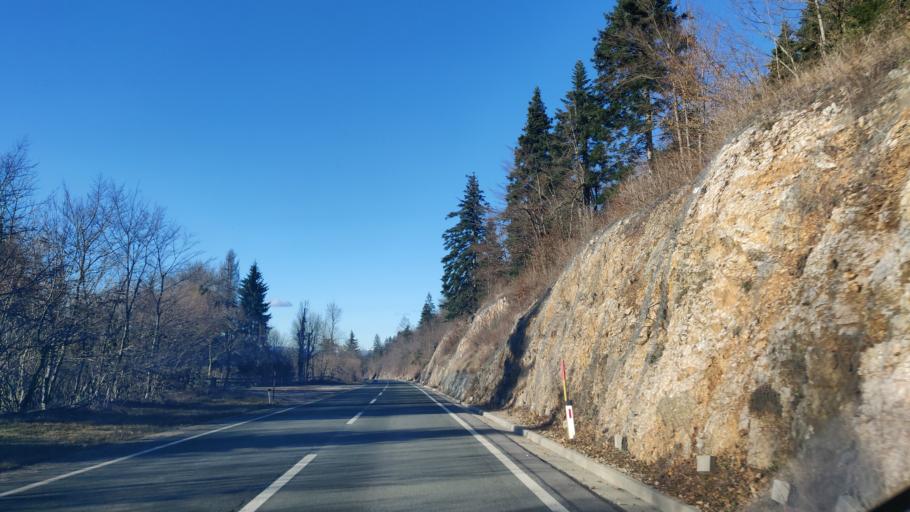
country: SI
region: Logatec
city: Logatec
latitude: 45.8863
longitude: 14.2008
